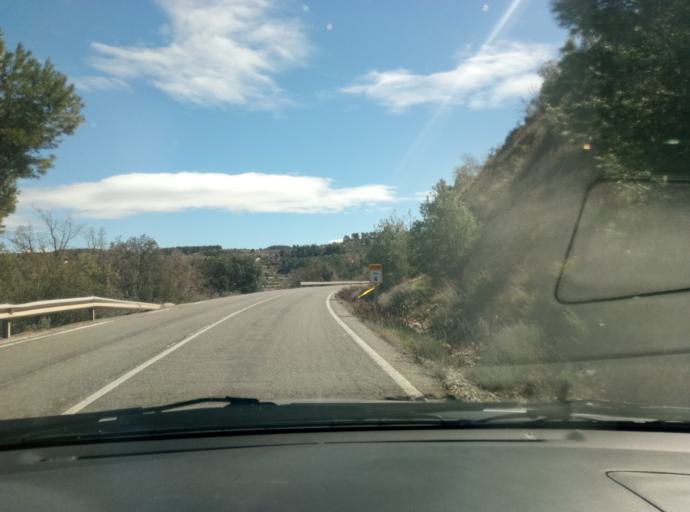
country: ES
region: Catalonia
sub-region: Provincia de Lleida
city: Vallbona de les Monges
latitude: 41.5356
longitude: 1.0722
